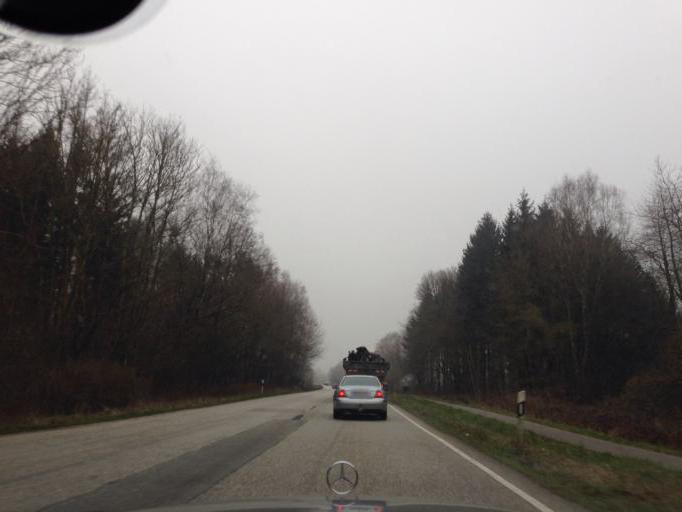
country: DE
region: Schleswig-Holstein
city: Klein Barkau
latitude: 54.2537
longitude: 10.1482
